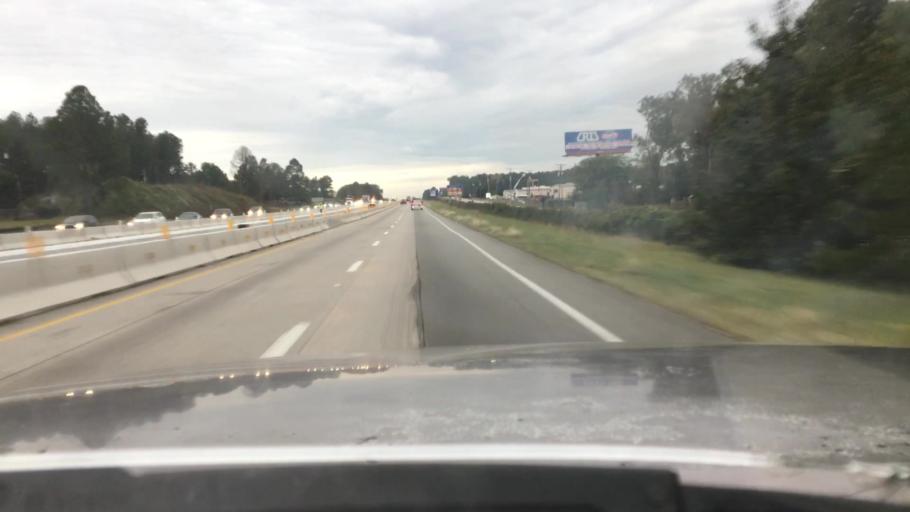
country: US
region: South Carolina
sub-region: Lexington County
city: Lexington
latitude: 33.9644
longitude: -81.2135
